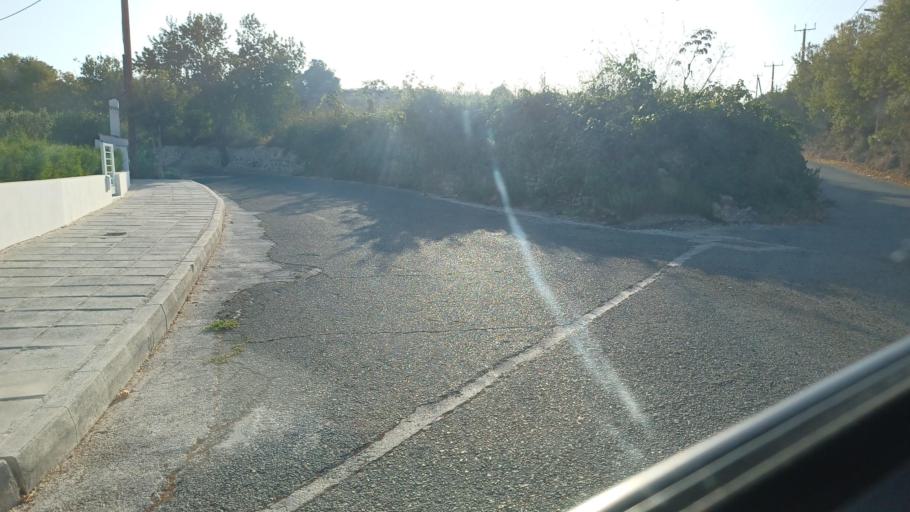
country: CY
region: Pafos
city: Mesogi
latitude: 34.8346
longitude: 32.4822
